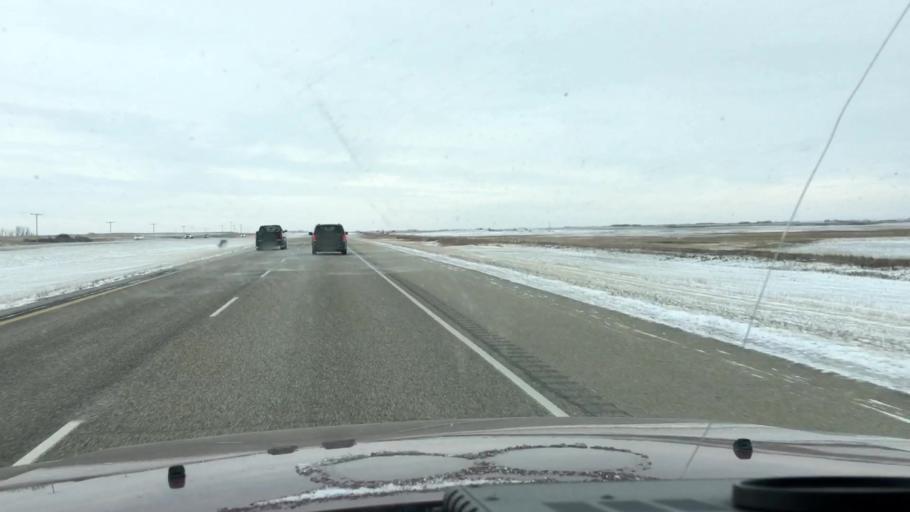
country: CA
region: Saskatchewan
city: Saskatoon
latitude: 51.5976
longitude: -106.3918
